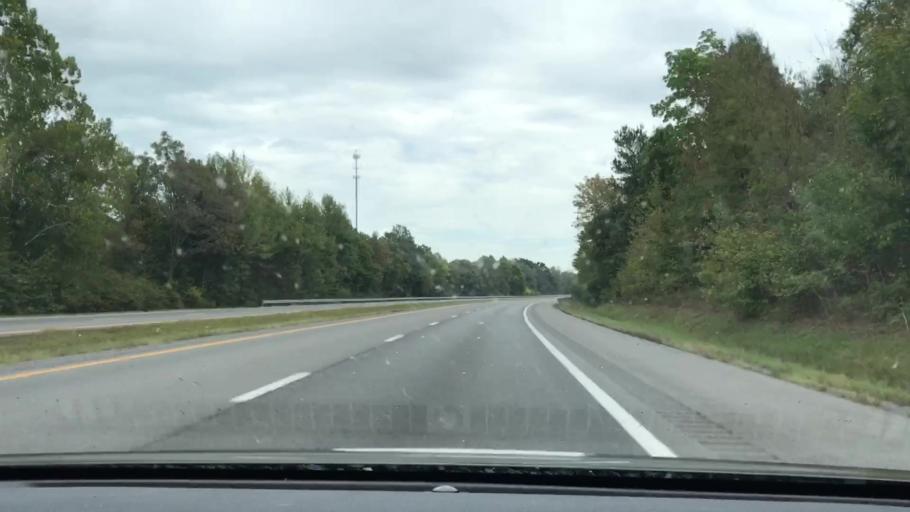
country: US
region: Kentucky
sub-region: Marshall County
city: Benton
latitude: 36.8196
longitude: -88.4810
